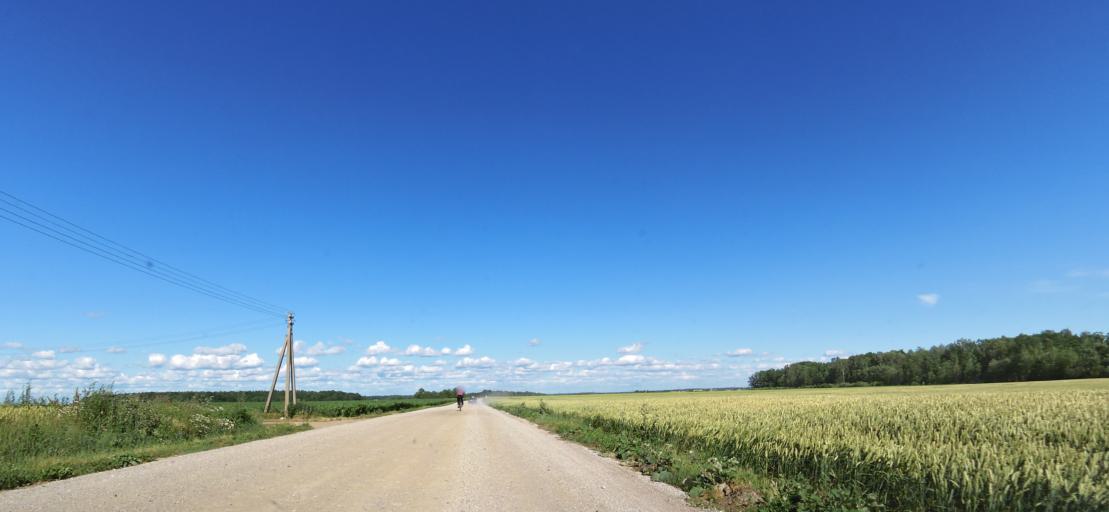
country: LT
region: Panevezys
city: Pasvalys
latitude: 56.1450
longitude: 24.4203
